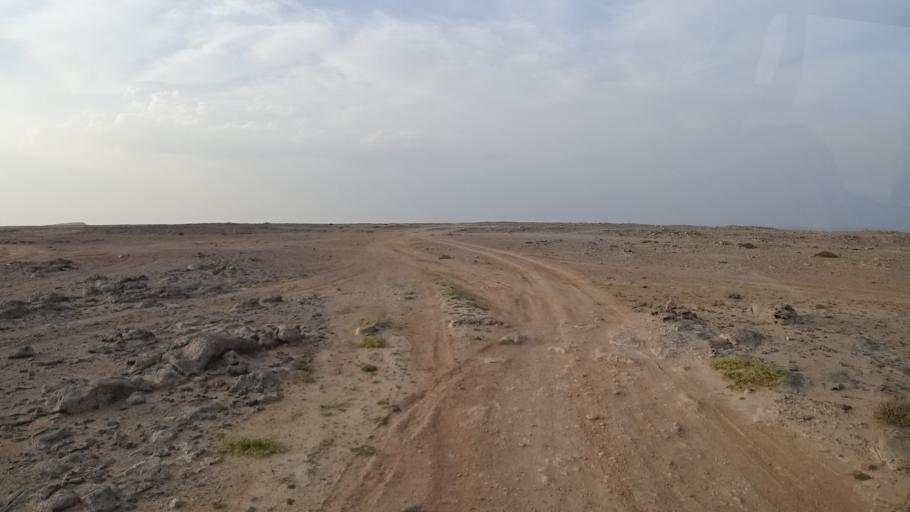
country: OM
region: Ash Sharqiyah
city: Sur
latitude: 22.4534
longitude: 59.8252
